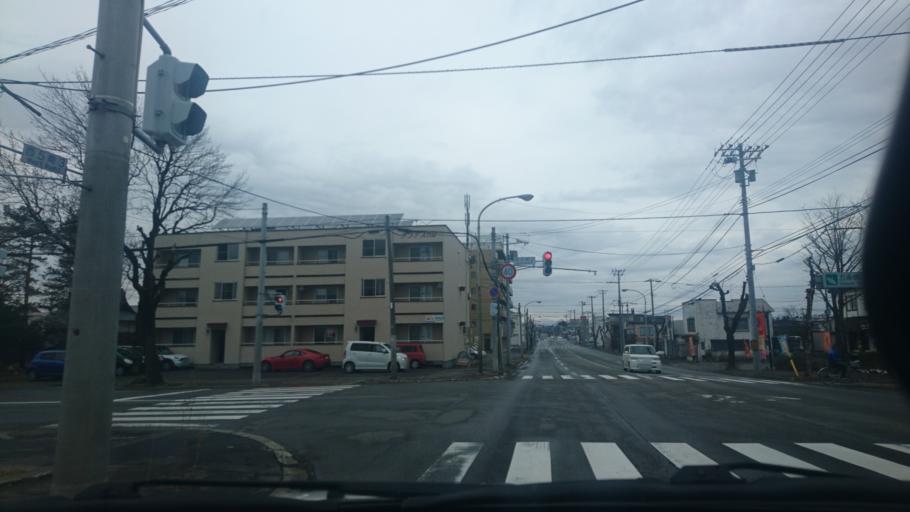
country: JP
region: Hokkaido
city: Obihiro
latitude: 42.9290
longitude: 143.1964
